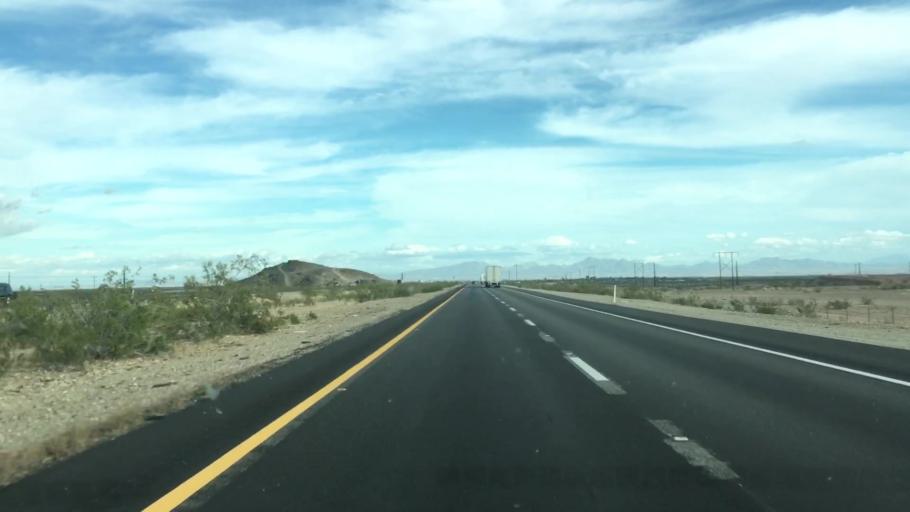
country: US
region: California
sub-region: Riverside County
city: Mesa Verde
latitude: 33.6086
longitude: -114.7681
